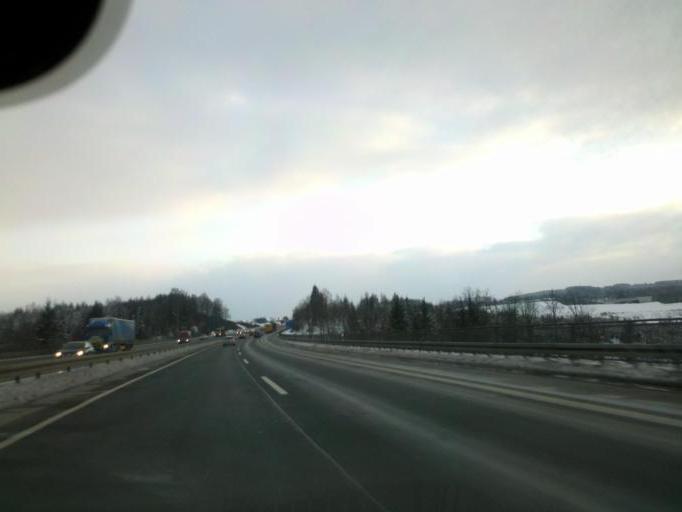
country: DE
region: North Rhine-Westphalia
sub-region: Regierungsbezirk Arnsberg
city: Olpe
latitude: 51.0298
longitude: 7.8248
